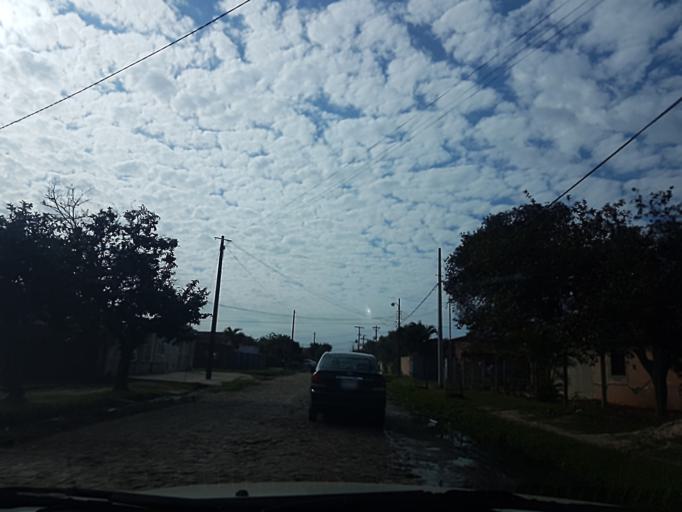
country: PY
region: Central
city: Colonia Mariano Roque Alonso
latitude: -25.2100
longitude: -57.5394
